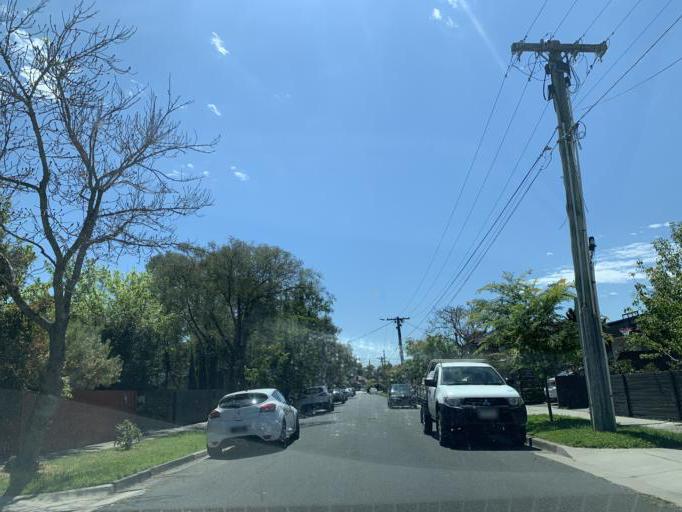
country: AU
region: Victoria
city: Highett
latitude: -37.9371
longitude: 145.0477
